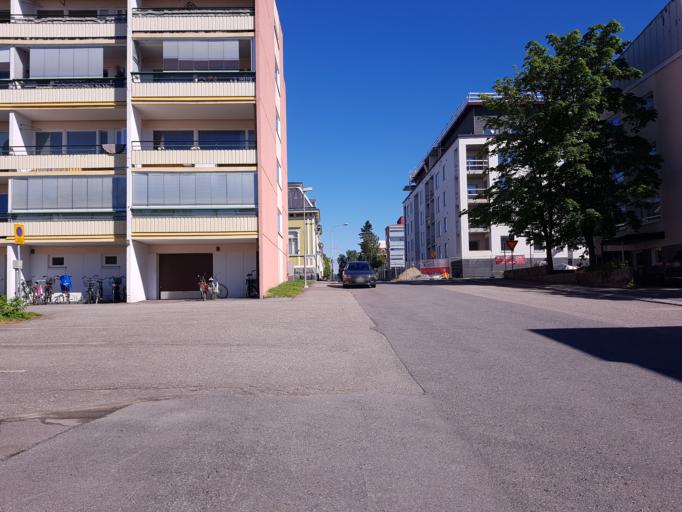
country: FI
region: Northern Savo
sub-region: Kuopio
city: Kuopio
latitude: 62.8878
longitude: 27.6861
